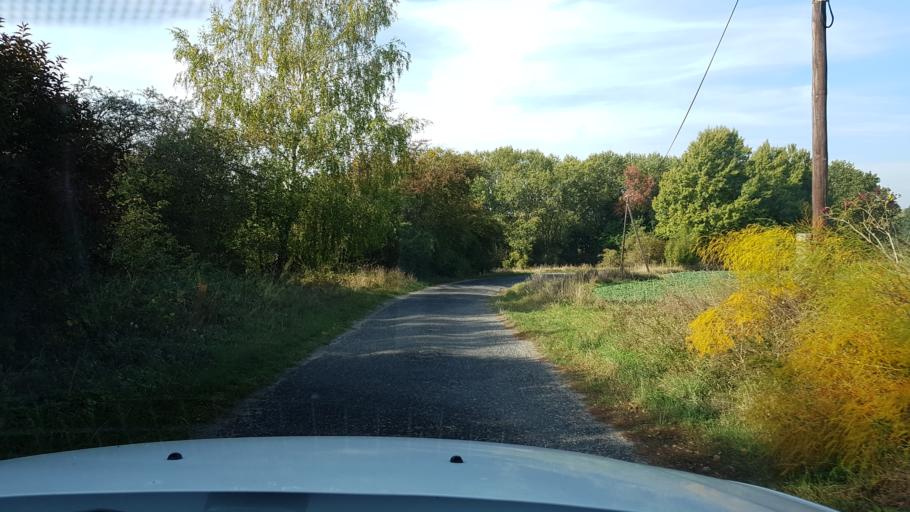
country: PL
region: West Pomeranian Voivodeship
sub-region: Powiat mysliborski
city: Mysliborz
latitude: 52.9366
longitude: 14.9297
